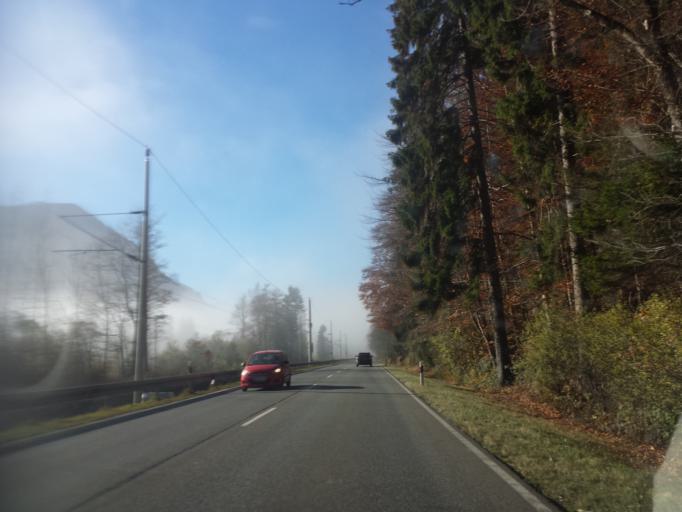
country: DE
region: Bavaria
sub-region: Upper Bavaria
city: Eschenlohe
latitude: 47.5795
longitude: 11.1663
